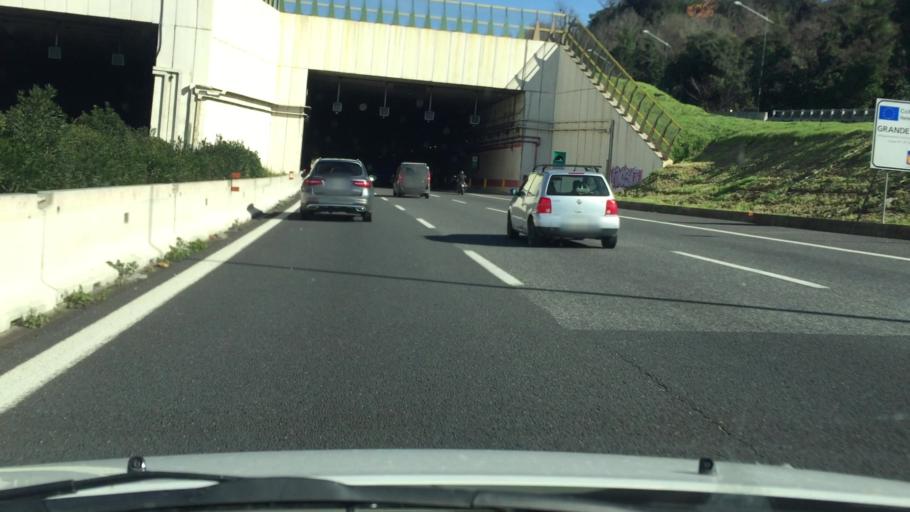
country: VA
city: Vatican City
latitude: 41.9743
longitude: 12.4218
